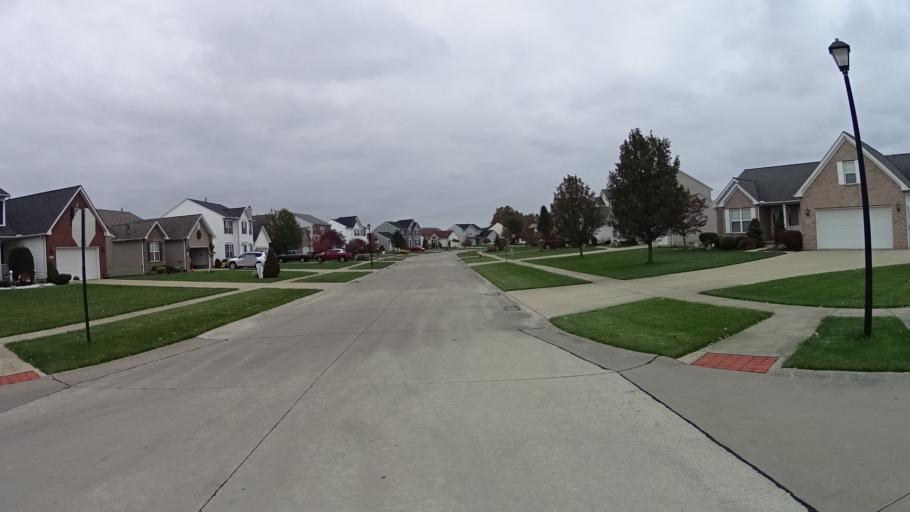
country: US
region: Ohio
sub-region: Lorain County
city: Lorain
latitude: 41.4409
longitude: -82.2206
